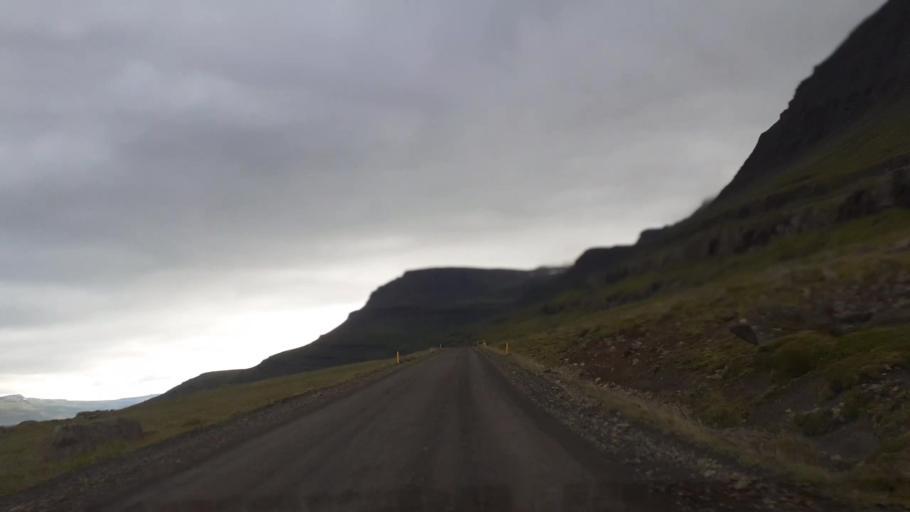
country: IS
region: East
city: Reydarfjoerdur
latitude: 65.0144
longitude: -14.1914
